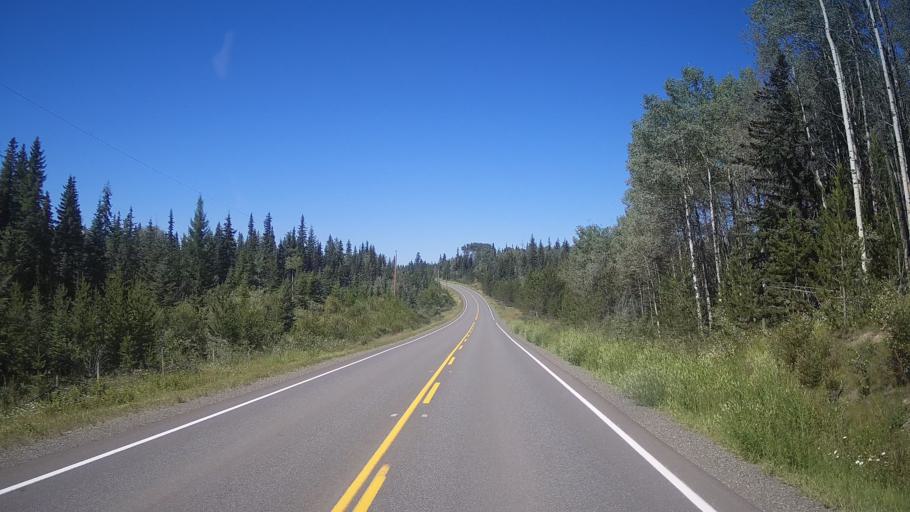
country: CA
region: British Columbia
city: Cache Creek
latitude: 51.5426
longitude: -120.9631
